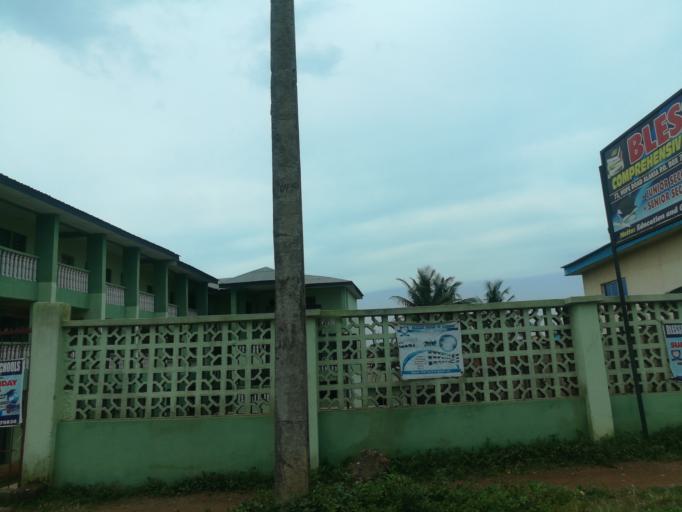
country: NG
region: Oyo
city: Ibadan
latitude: 7.3844
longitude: 3.9652
